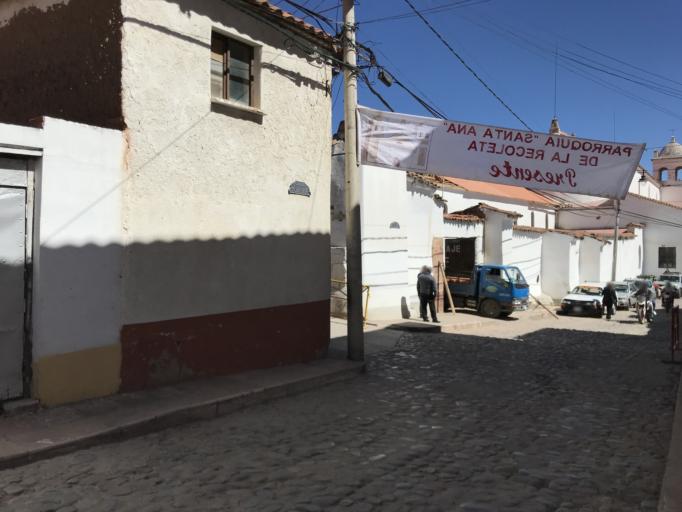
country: BO
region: Chuquisaca
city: Sucre
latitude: -19.0549
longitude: -65.2525
